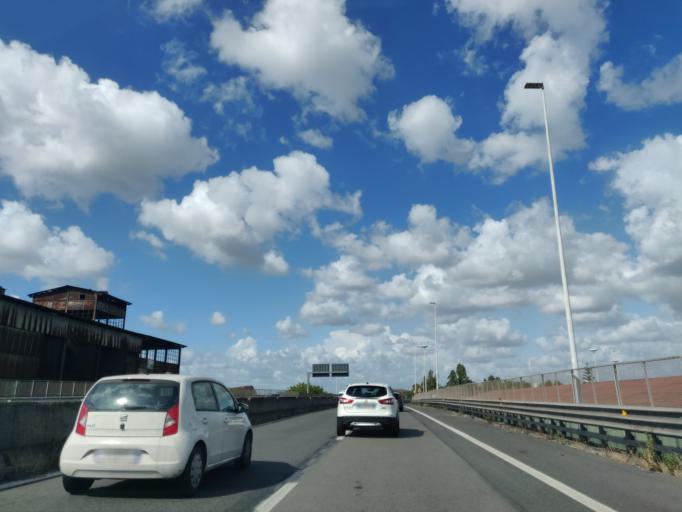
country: VA
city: Vatican City
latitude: 41.8394
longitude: 12.4515
